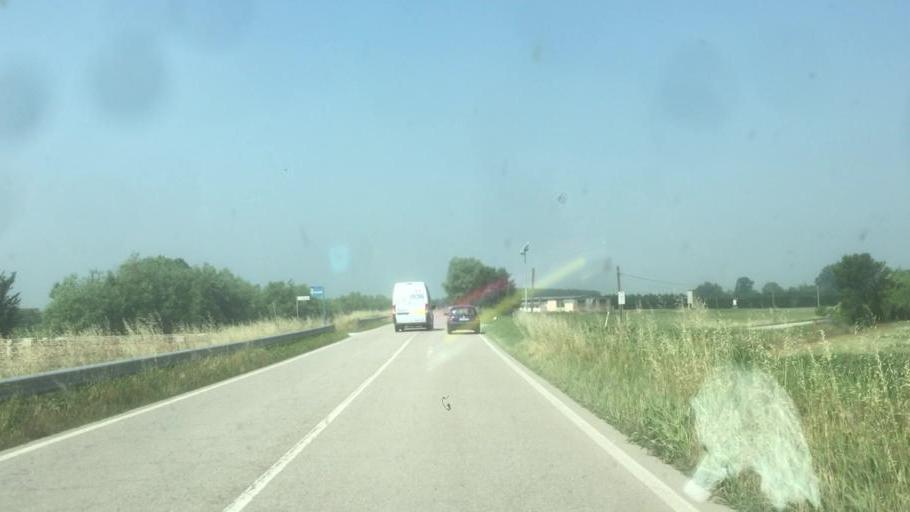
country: IT
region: Lombardy
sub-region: Provincia di Mantova
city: Revere
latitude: 45.0346
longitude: 11.1575
